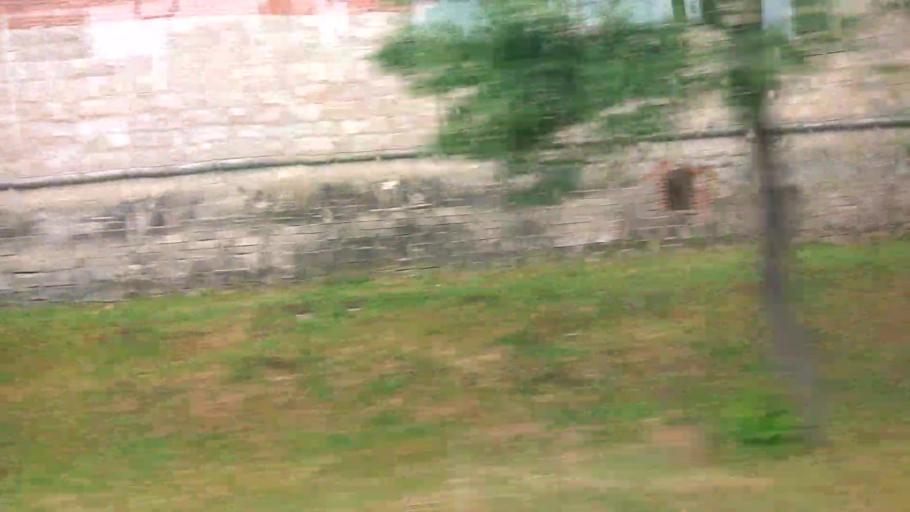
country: RU
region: Moskovskaya
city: Zaraysk
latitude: 54.7569
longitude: 38.8734
